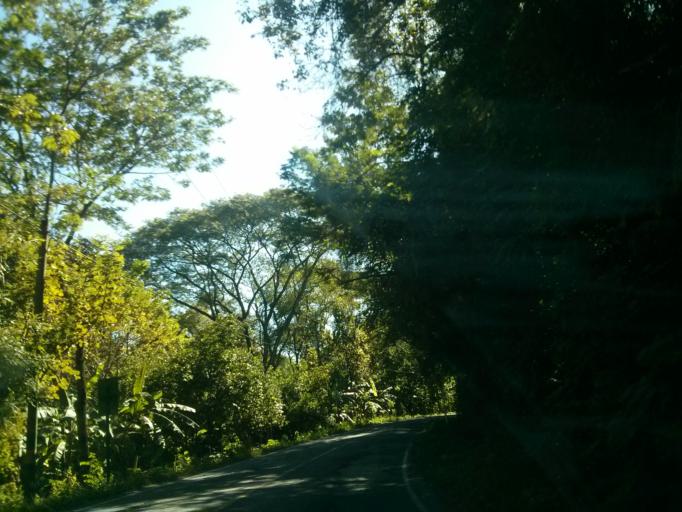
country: CR
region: Puntarenas
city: Paquera
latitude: 9.8232
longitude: -84.9154
